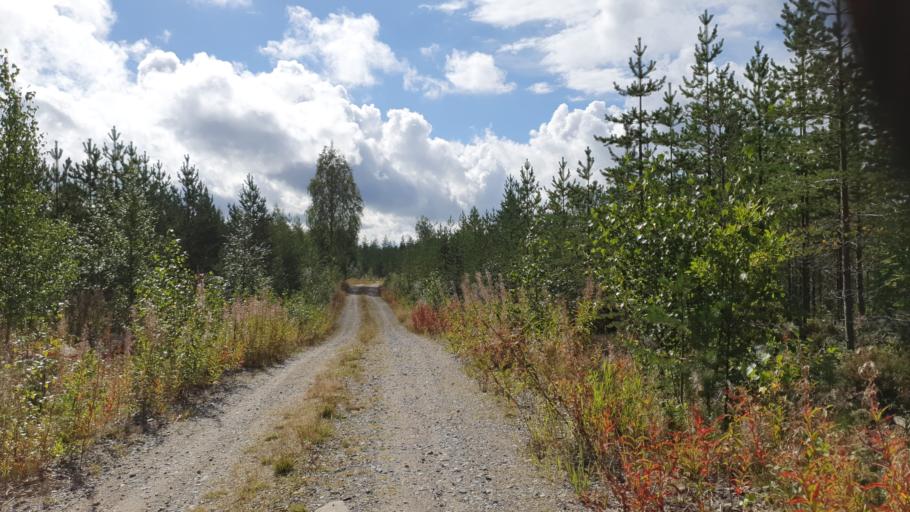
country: FI
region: Kainuu
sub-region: Kehys-Kainuu
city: Kuhmo
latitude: 64.1474
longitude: 29.3881
